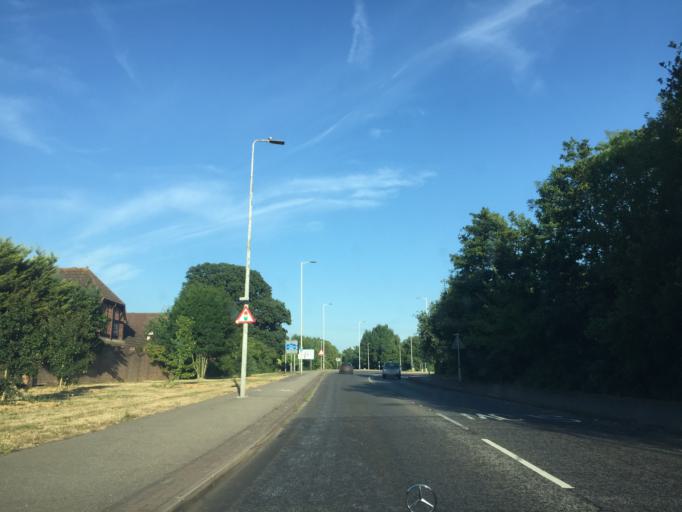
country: GB
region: England
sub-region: Bracknell Forest
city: Sandhurst
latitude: 51.3392
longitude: -0.7823
